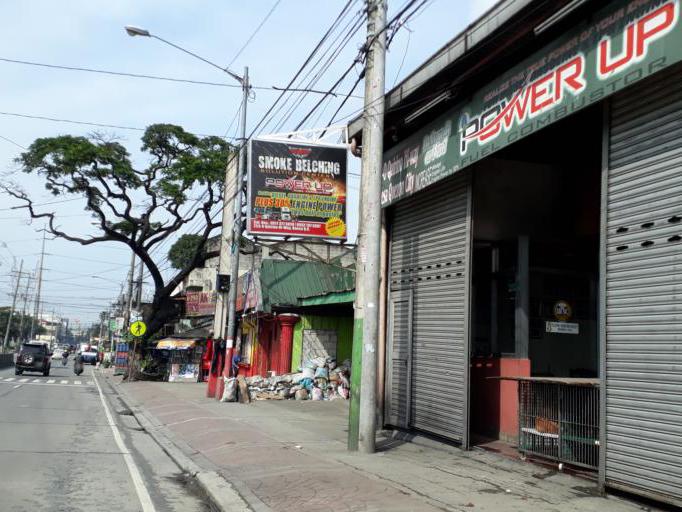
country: PH
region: Calabarzon
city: Bagong Pagasa
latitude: 14.6739
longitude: 121.0136
